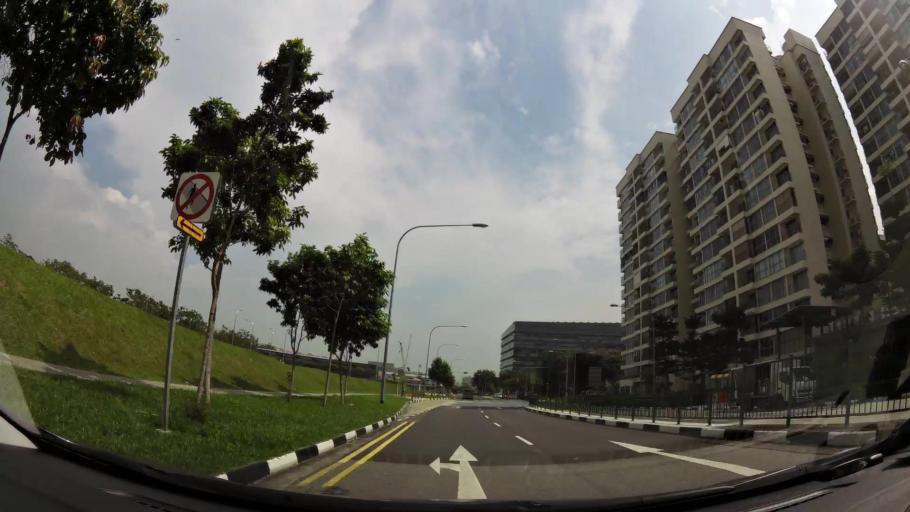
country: SG
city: Singapore
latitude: 1.3579
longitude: 103.9405
